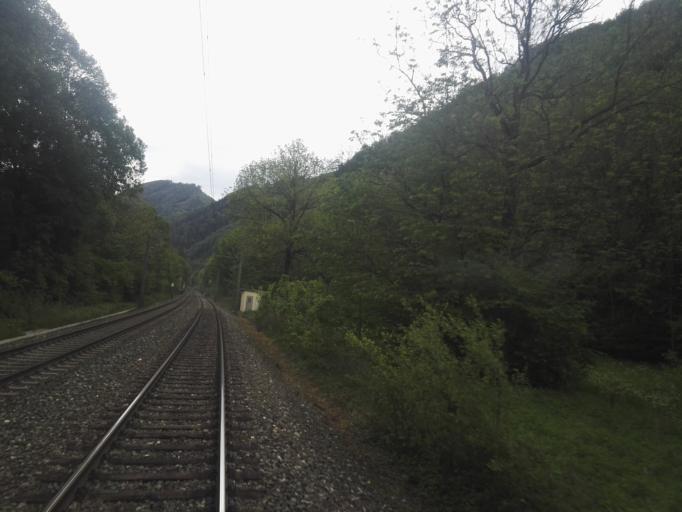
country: AT
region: Styria
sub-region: Politischer Bezirk Graz-Umgebung
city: Rothelstein
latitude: 47.2990
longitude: 15.3575
